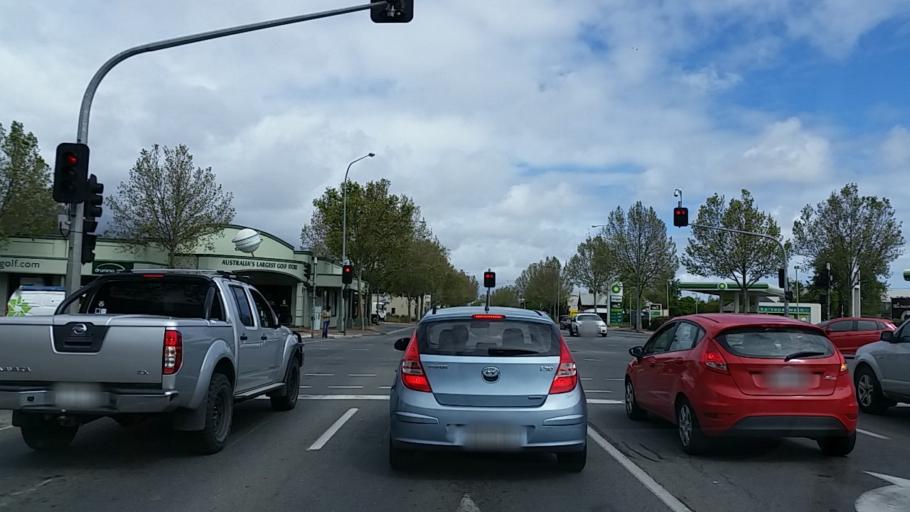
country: AU
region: South Australia
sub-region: City of West Torrens
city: Thebarton
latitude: -34.9235
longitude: 138.5698
